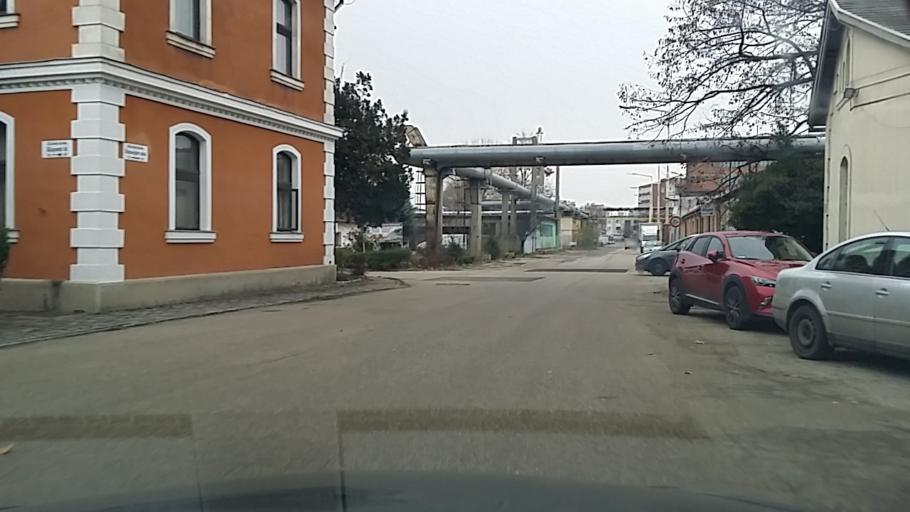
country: HU
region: Budapest
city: Budapest XXI. keruelet
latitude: 47.4274
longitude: 19.0583
